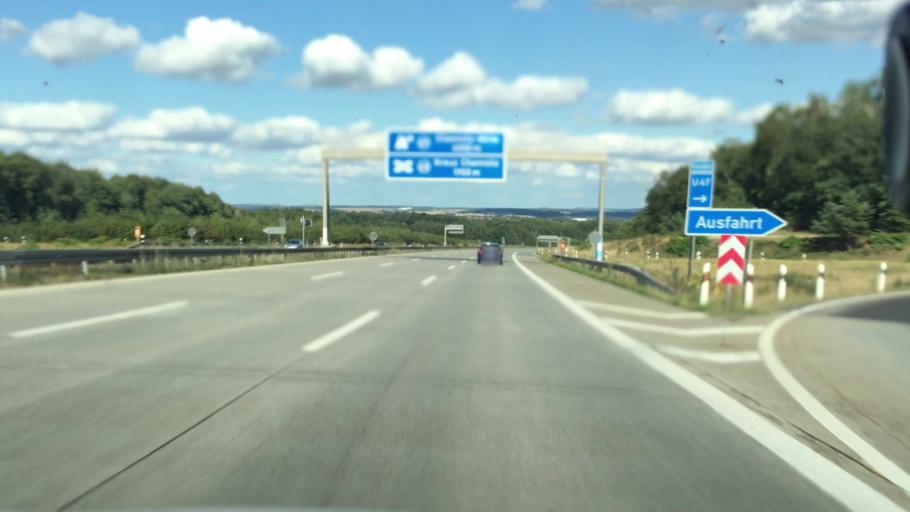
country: DE
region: Saxony
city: Limbach-Oberfrohna
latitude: 50.8456
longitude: 12.8063
